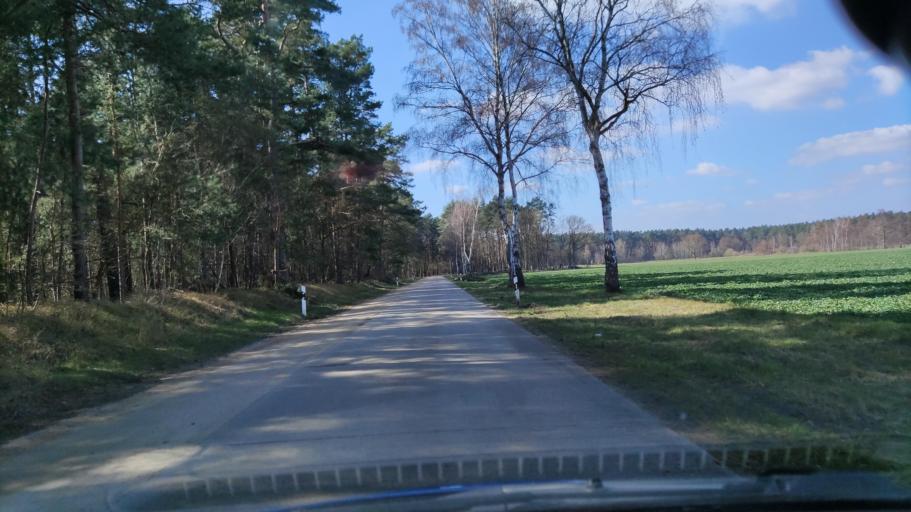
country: DE
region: Lower Saxony
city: Trebel
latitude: 52.9947
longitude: 11.3019
